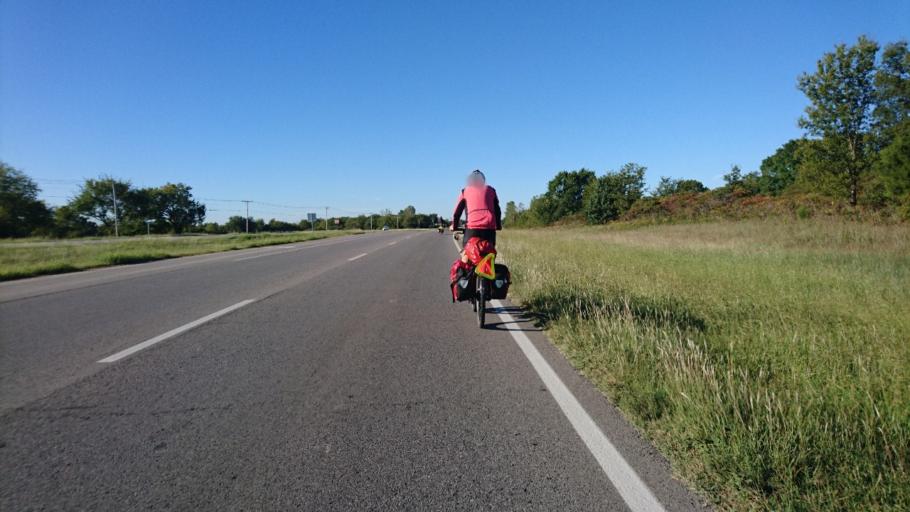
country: US
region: Oklahoma
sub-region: Rogers County
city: Claremore
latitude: 36.2729
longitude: -95.6440
